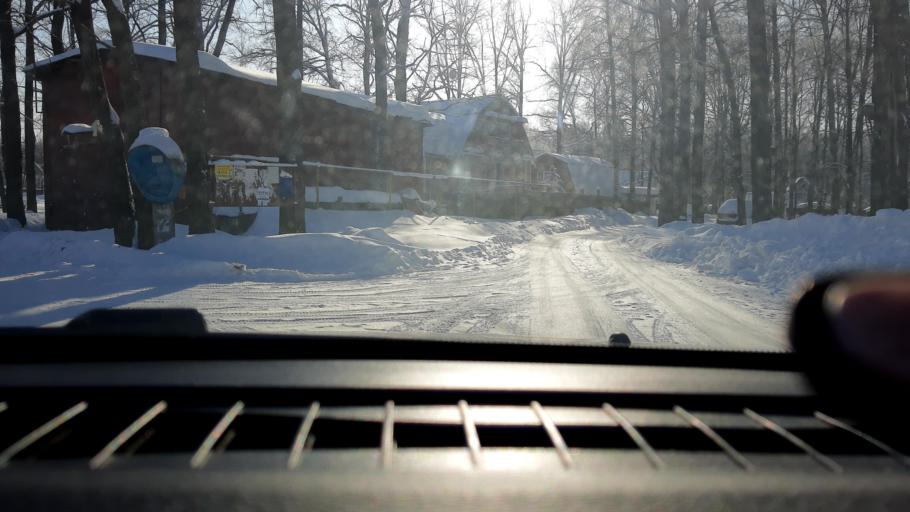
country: RU
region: Nizjnij Novgorod
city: Afonino
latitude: 56.1992
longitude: 44.0328
